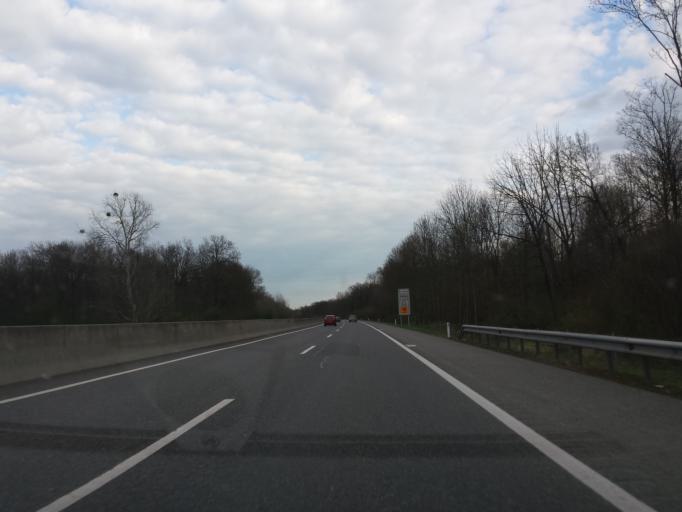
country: AT
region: Lower Austria
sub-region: Politischer Bezirk Tulln
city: Kirchberg am Wagram
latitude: 48.3749
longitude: 15.9319
